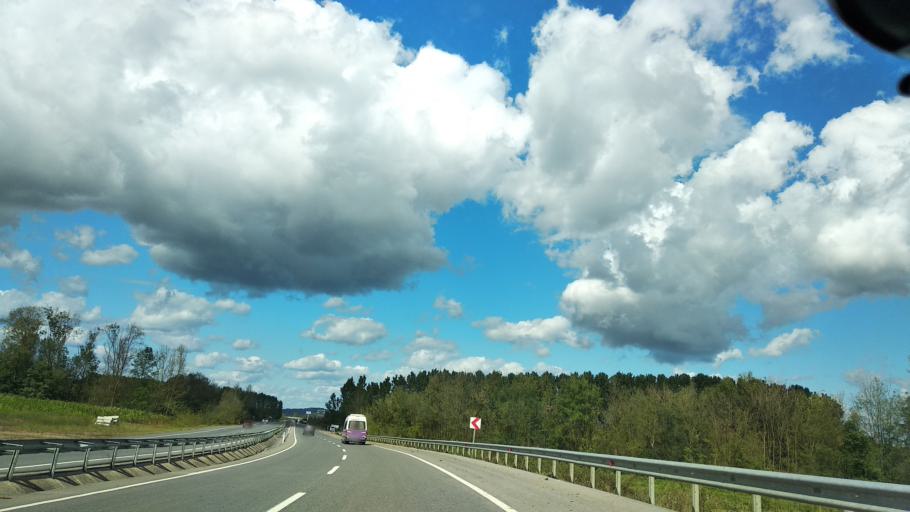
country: TR
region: Sakarya
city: Ortakoy
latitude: 41.0089
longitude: 30.6130
